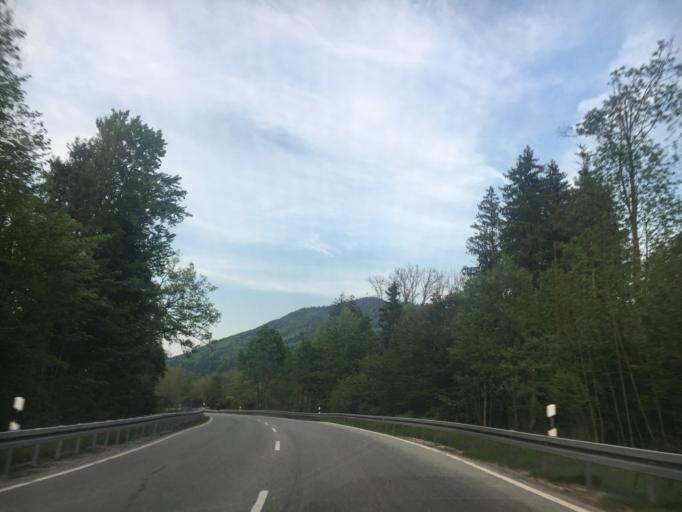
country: DE
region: Bavaria
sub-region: Upper Bavaria
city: Bichl
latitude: 47.7256
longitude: 11.4224
